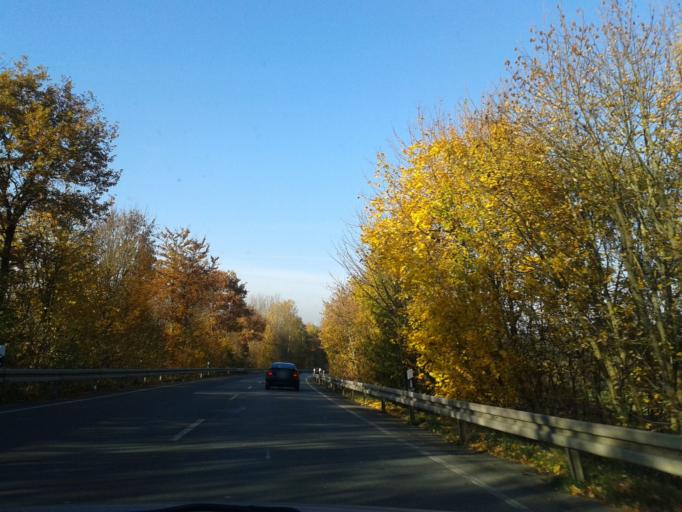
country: DE
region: North Rhine-Westphalia
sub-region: Regierungsbezirk Arnsberg
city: Ruthen
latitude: 51.4756
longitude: 8.4470
